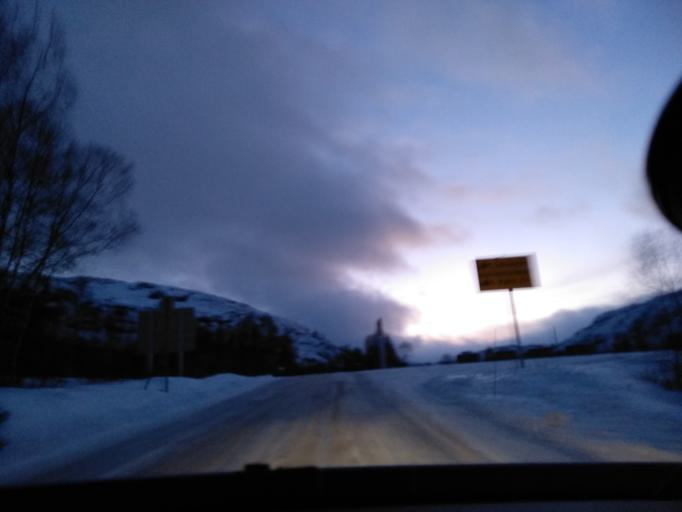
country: NO
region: Vest-Agder
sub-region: Sirdal
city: Tonstad
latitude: 59.0127
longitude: 6.9387
